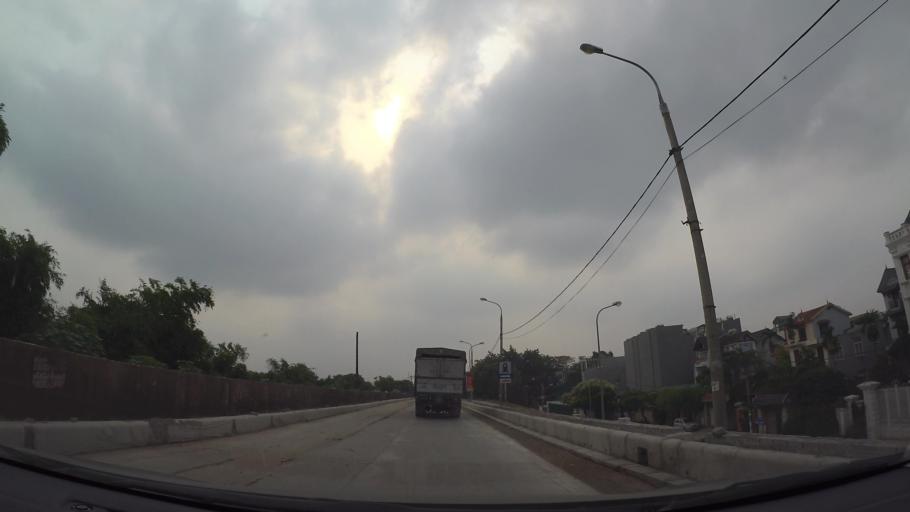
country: VN
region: Ha Noi
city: Trau Quy
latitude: 21.0213
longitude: 105.8968
